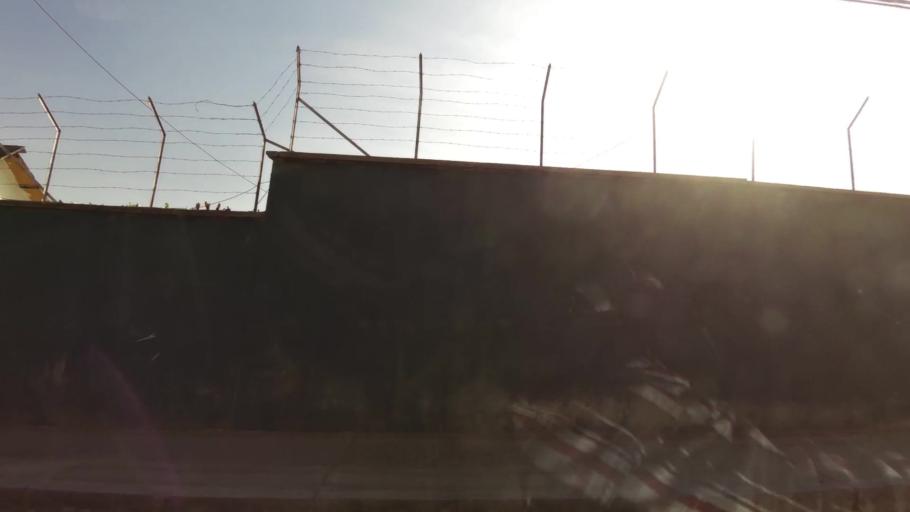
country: BO
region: La Paz
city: La Paz
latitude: -16.5027
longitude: -68.0830
